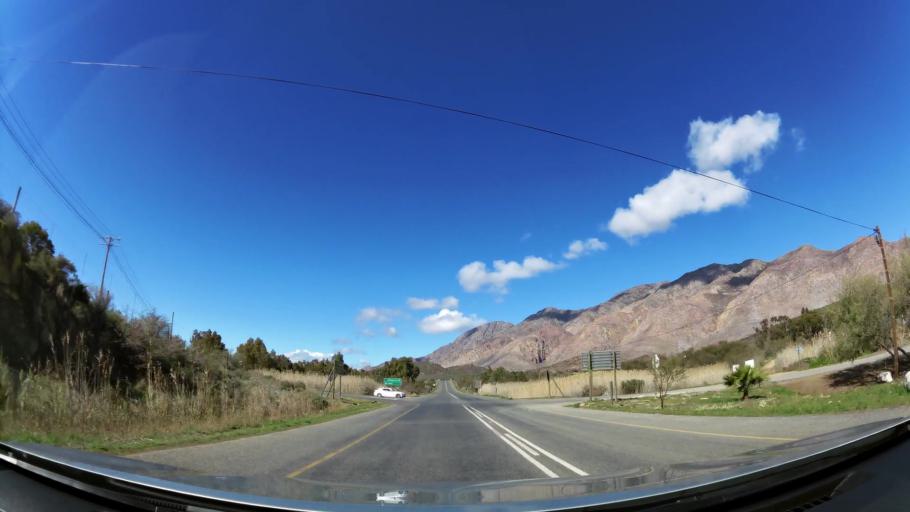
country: ZA
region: Western Cape
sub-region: Cape Winelands District Municipality
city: Ashton
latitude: -33.7915
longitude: 20.1372
